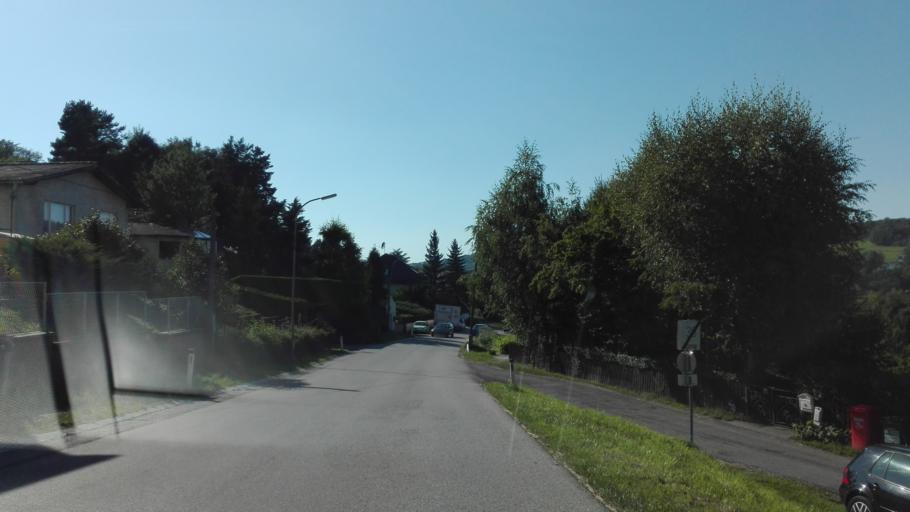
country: AT
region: Lower Austria
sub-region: Politischer Bezirk Sankt Polten
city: Eichgraben
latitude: 48.1615
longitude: 15.9671
